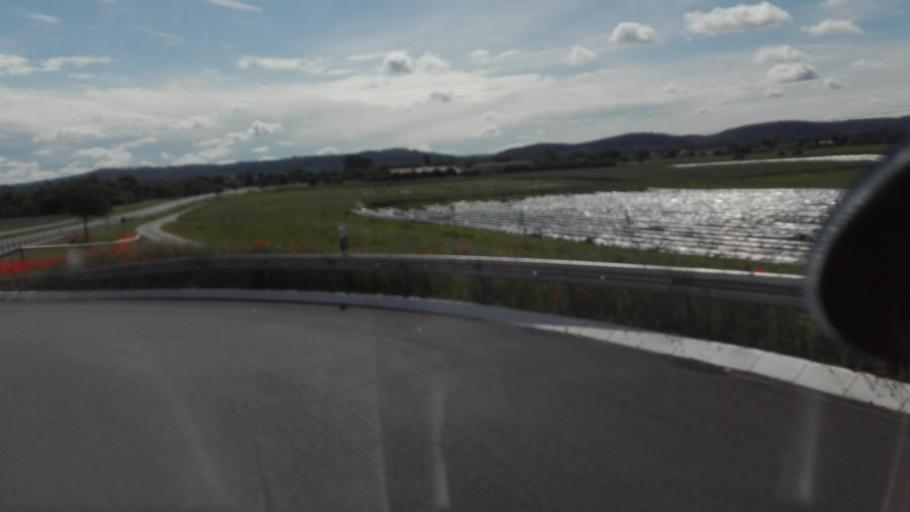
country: DE
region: Baden-Wuerttemberg
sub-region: Karlsruhe Region
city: Karlsdorf-Neuthard
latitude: 49.0971
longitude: 8.4935
